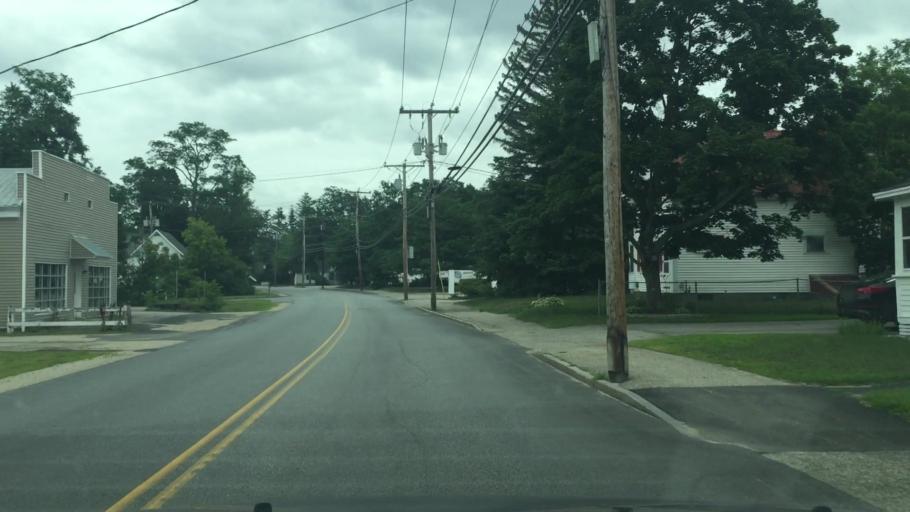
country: US
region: New Hampshire
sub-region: Carroll County
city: Conway
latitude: 43.9752
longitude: -71.1332
